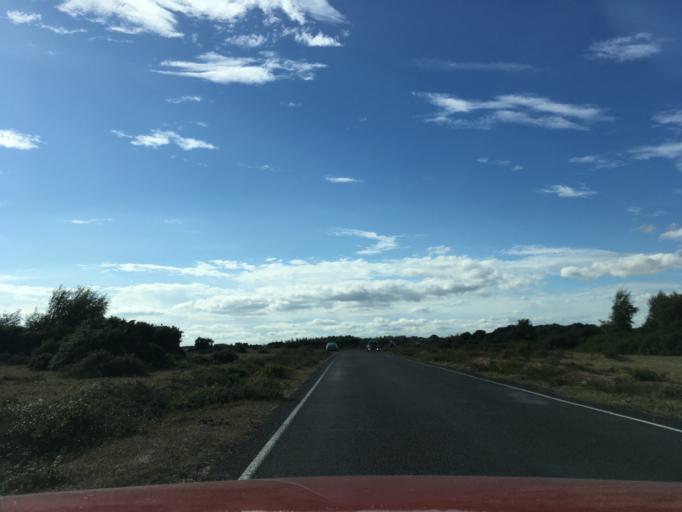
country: GB
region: England
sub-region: Hampshire
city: Cadnam
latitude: 50.9085
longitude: -1.6443
